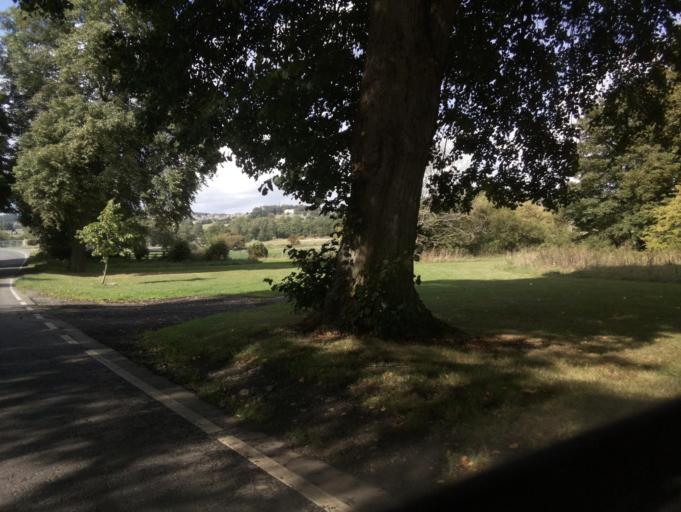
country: GB
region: England
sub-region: North Yorkshire
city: Leyburn
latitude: 54.2915
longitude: -1.8142
